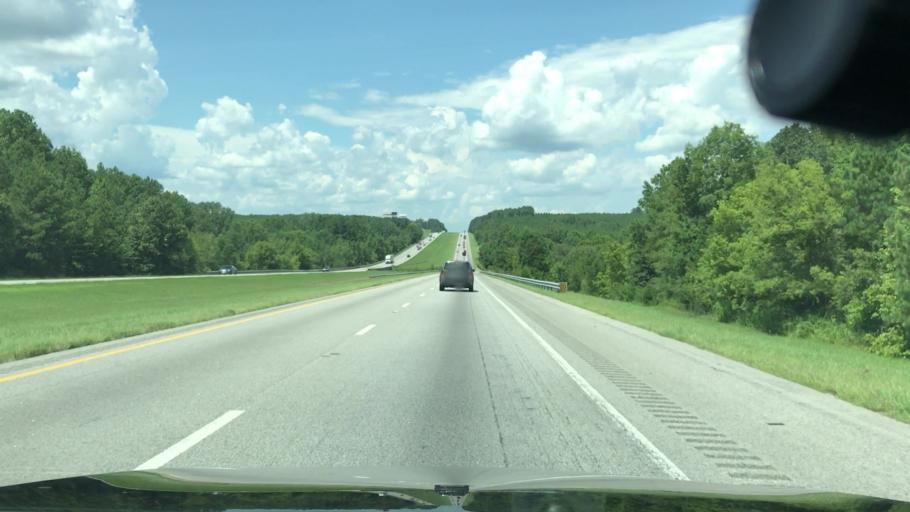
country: US
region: South Carolina
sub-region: Chester County
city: Great Falls
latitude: 34.5843
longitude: -81.0139
